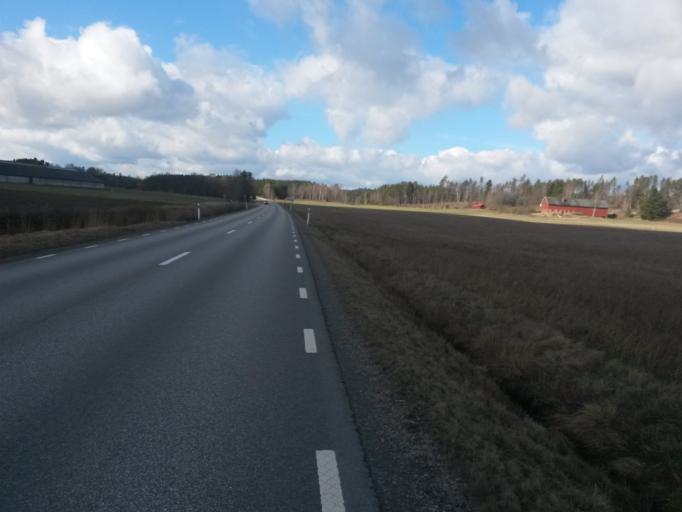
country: SE
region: Vaestra Goetaland
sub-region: Vargarda Kommun
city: Jonstorp
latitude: 58.0614
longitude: 12.7294
